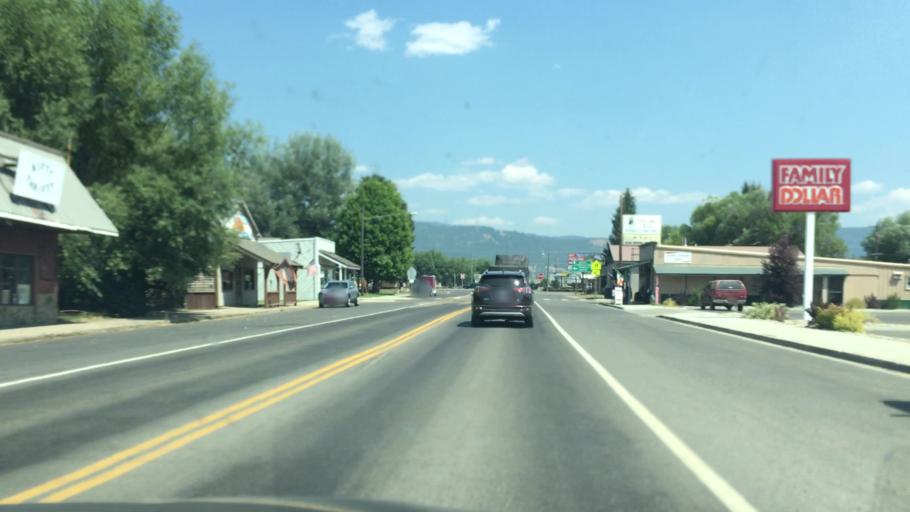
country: US
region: Idaho
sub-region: Valley County
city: McCall
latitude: 44.9711
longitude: -116.2839
